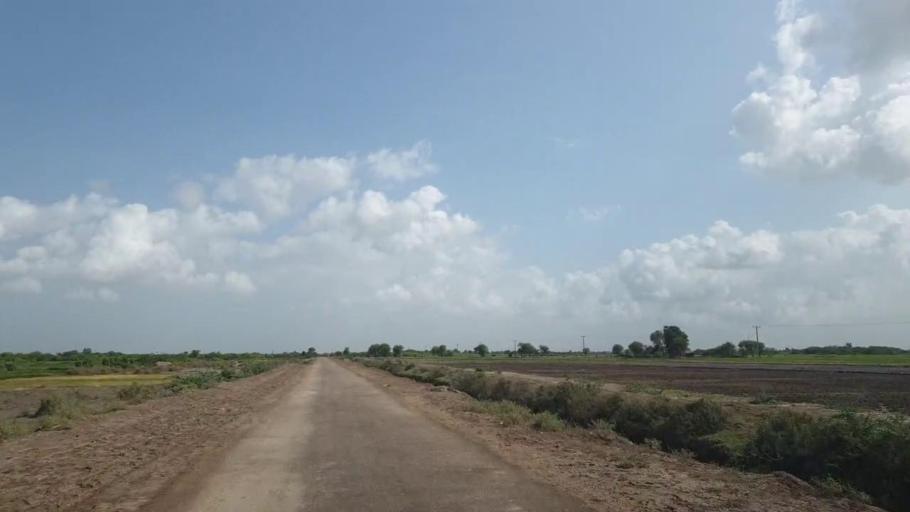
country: PK
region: Sindh
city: Kadhan
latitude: 24.5672
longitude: 69.0675
